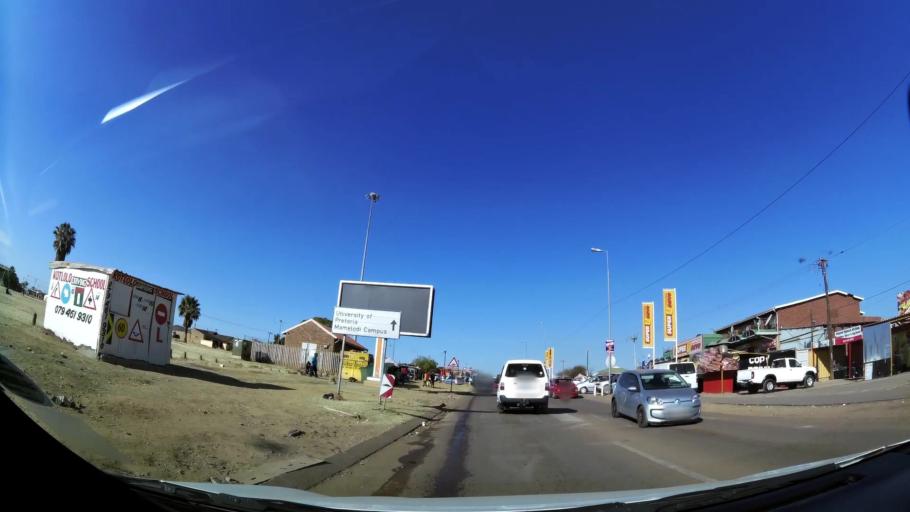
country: ZA
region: Gauteng
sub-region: City of Tshwane Metropolitan Municipality
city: Cullinan
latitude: -25.7212
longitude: 28.3850
